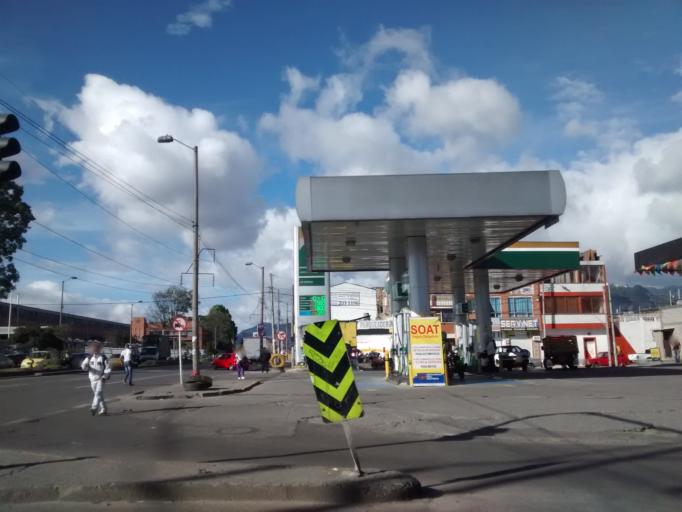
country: CO
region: Bogota D.C.
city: Bogota
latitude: 4.5944
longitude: -74.1123
